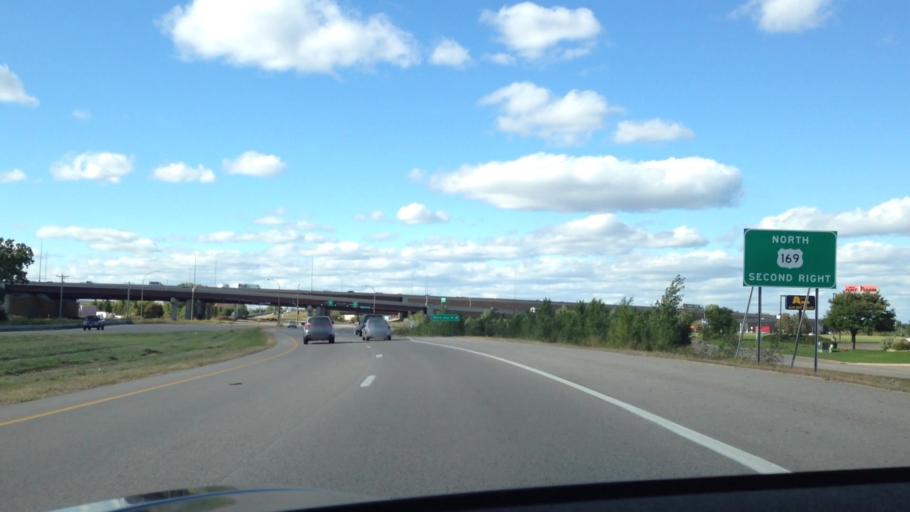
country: US
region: Minnesota
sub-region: Hennepin County
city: Osseo
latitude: 45.1031
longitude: -93.3905
